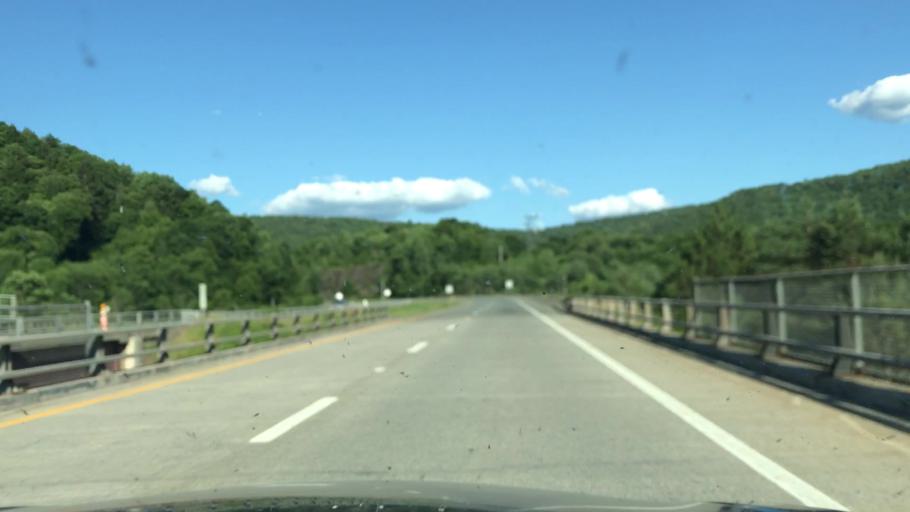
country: US
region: New York
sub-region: Sullivan County
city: Livingston Manor
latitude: 41.9502
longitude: -74.9654
